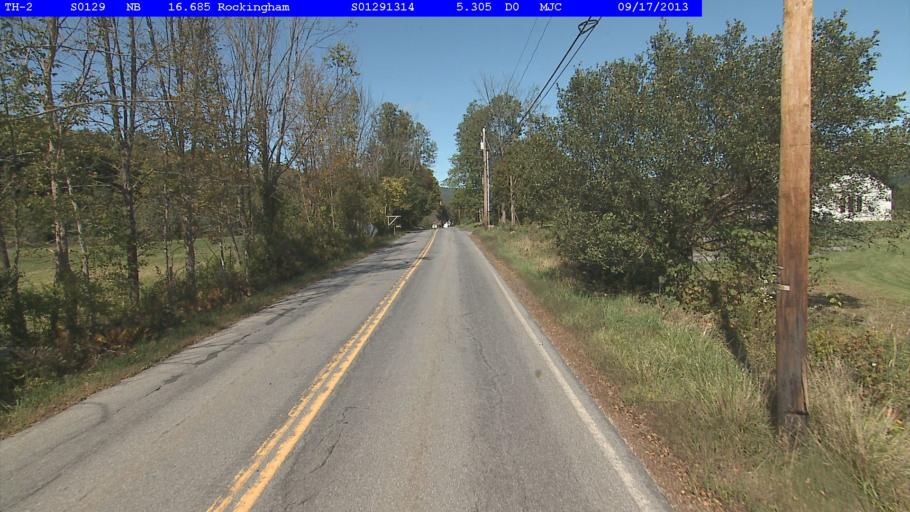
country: US
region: Vermont
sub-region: Windham County
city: Rockingham
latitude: 43.1928
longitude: -72.5115
